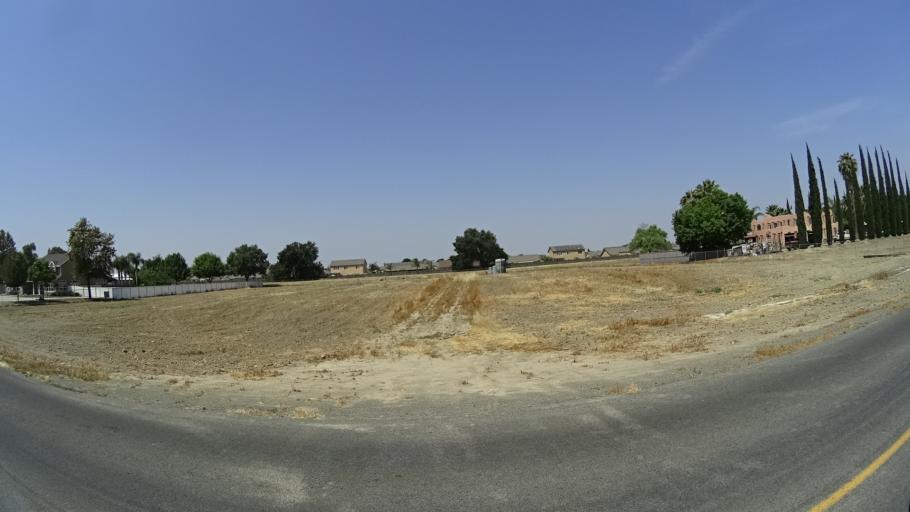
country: US
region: California
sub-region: Kings County
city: Lemoore
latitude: 36.3087
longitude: -119.7628
